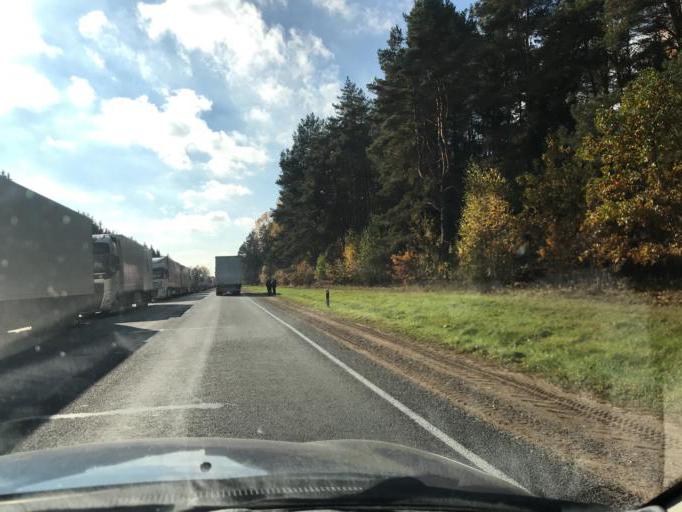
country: LT
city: Salcininkai
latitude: 54.2274
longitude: 25.3577
